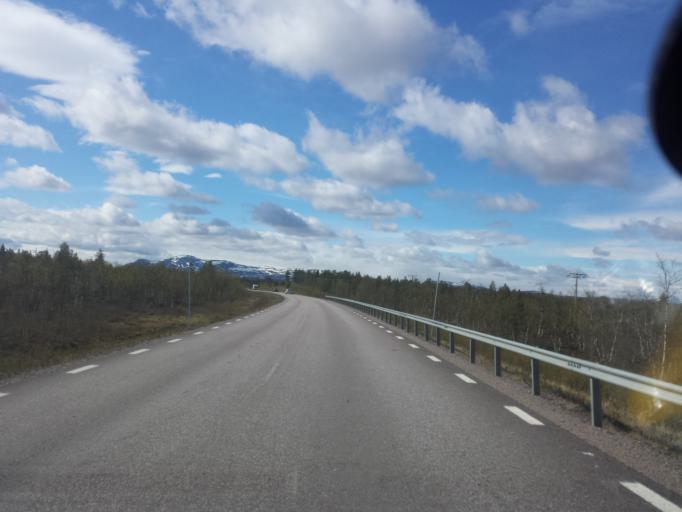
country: SE
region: Norrbotten
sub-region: Kiruna Kommun
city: Kiruna
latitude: 67.9879
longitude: 19.9342
